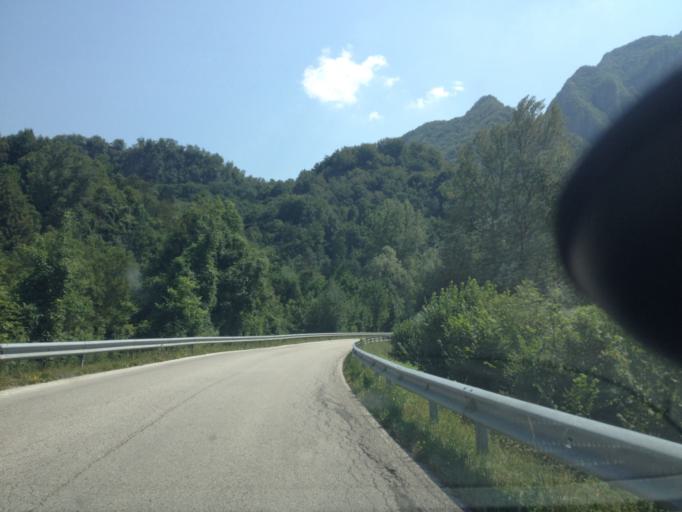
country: IT
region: Veneto
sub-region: Provincia di Vicenza
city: Arsiero
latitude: 45.8114
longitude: 11.3216
